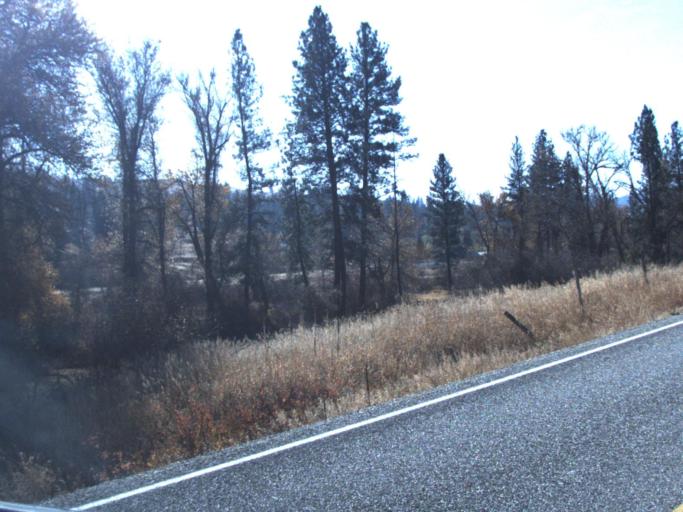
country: CA
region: British Columbia
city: Grand Forks
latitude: 48.8916
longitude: -118.5975
